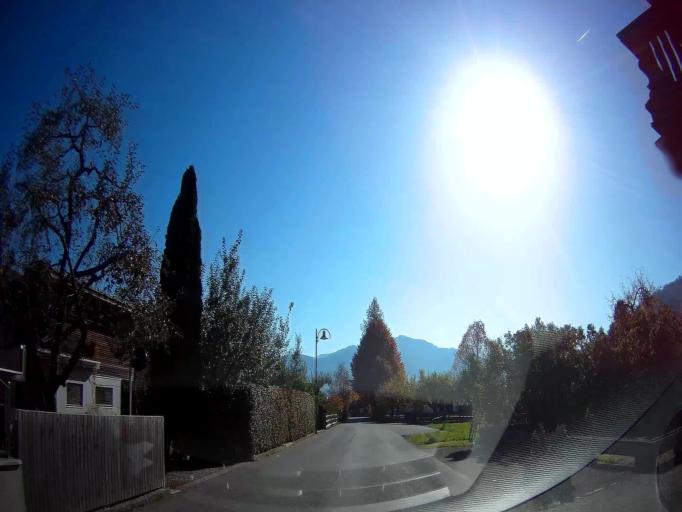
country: AT
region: Salzburg
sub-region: Politischer Bezirk Zell am See
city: Saalfelden am Steinernen Meer
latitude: 47.4471
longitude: 12.8155
